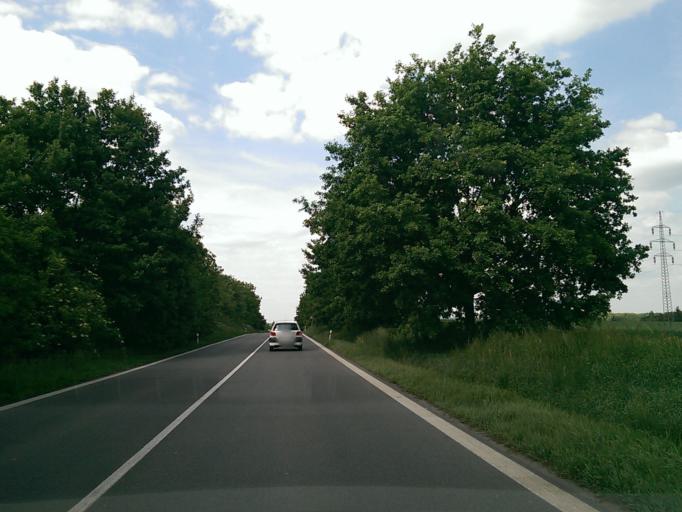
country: CZ
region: Central Bohemia
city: Libis
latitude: 50.2606
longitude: 14.4960
